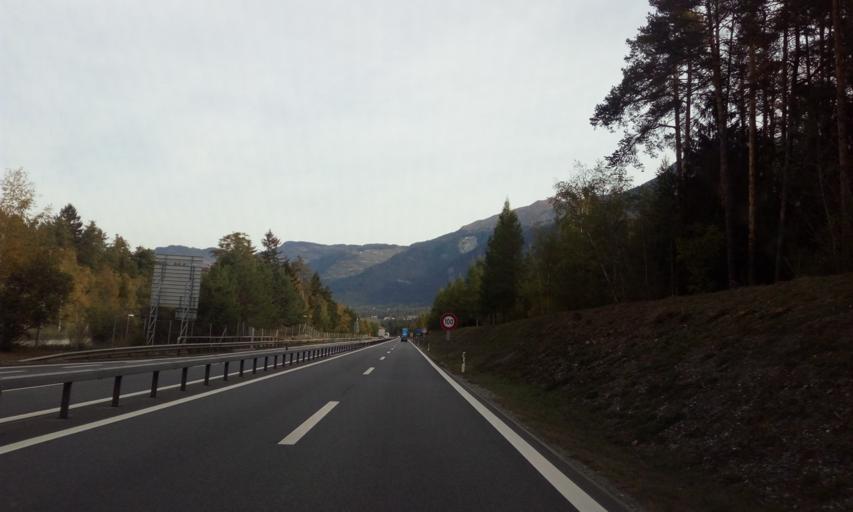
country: CH
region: Grisons
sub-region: Hinterrhein District
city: Thusis
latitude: 46.7008
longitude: 9.4474
